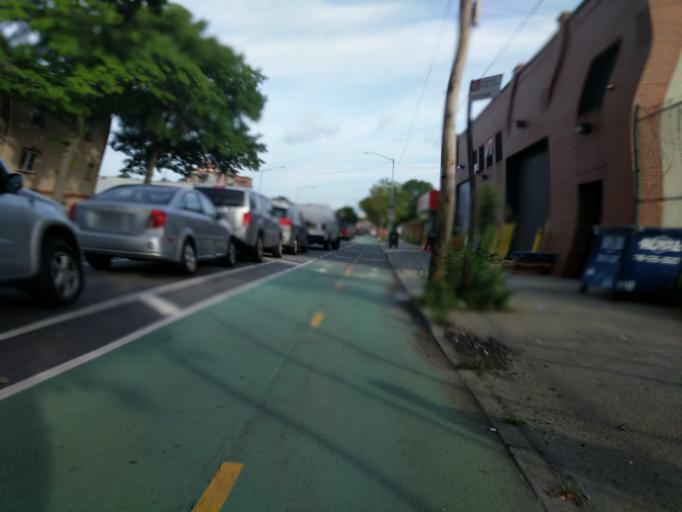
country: US
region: New York
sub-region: Queens County
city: Long Island City
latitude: 40.7787
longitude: -73.9048
